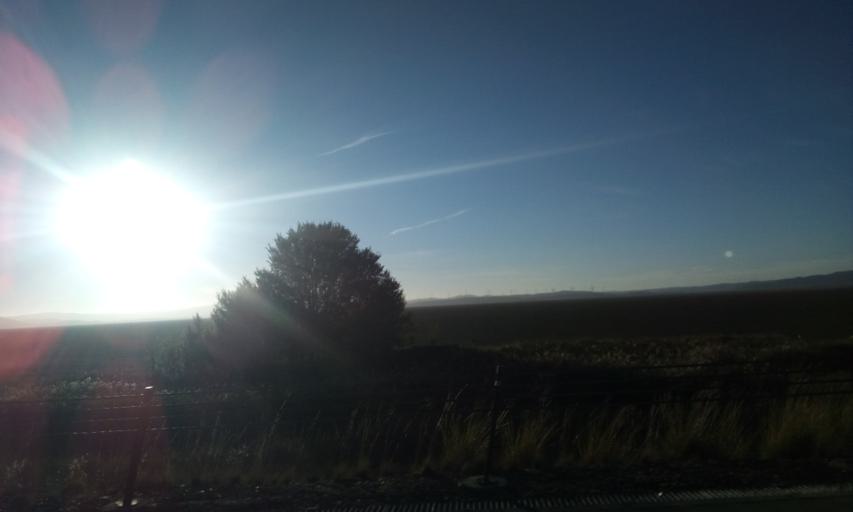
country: AU
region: New South Wales
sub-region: Yass Valley
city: Gundaroo
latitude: -35.0802
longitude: 149.3747
